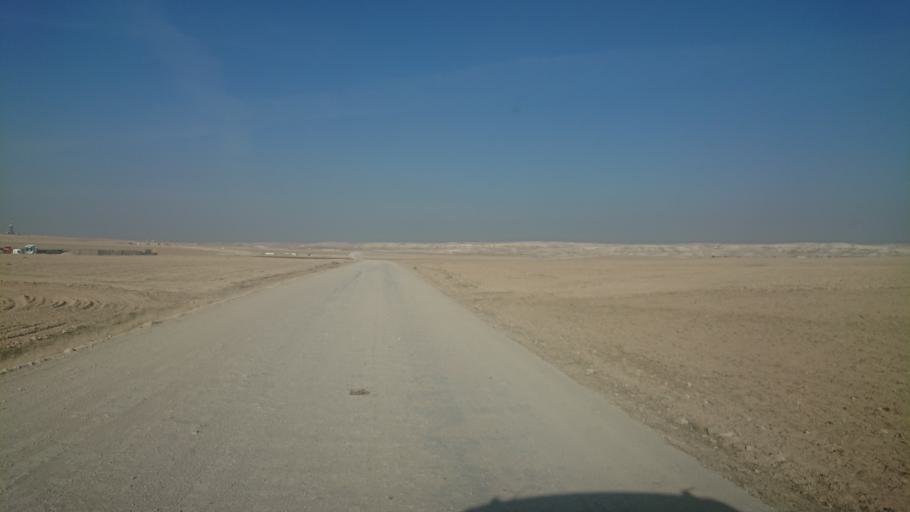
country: TR
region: Aksaray
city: Sultanhani
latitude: 38.0610
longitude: 33.6146
